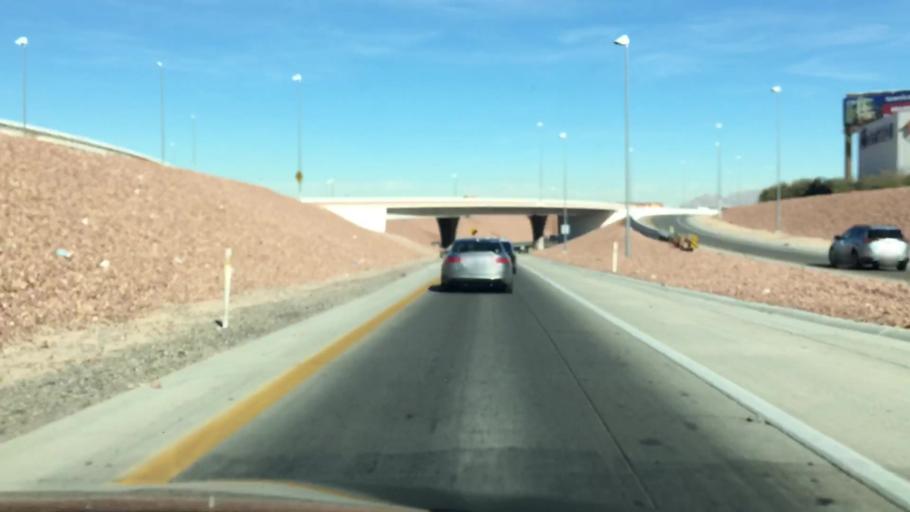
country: US
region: Nevada
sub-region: Clark County
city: Paradise
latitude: 36.0608
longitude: -115.1790
